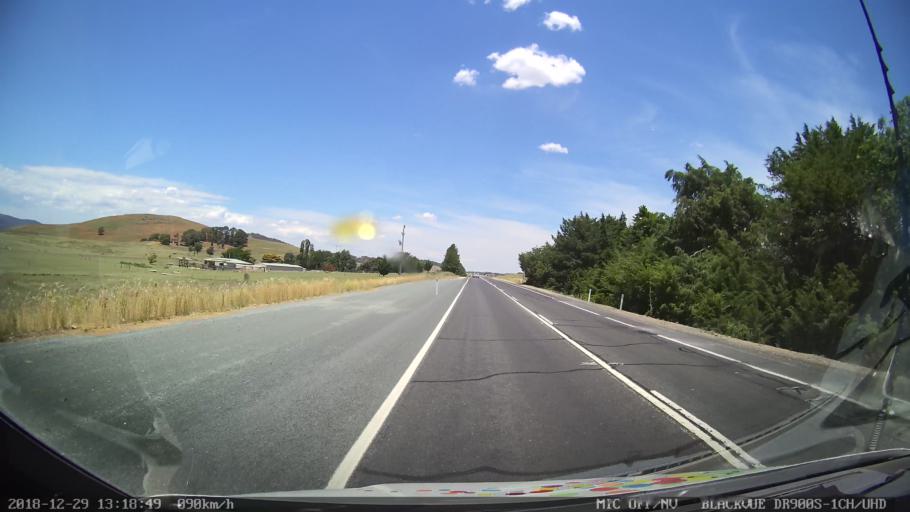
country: AU
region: Australian Capital Territory
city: Macarthur
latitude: -35.7565
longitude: 149.1611
